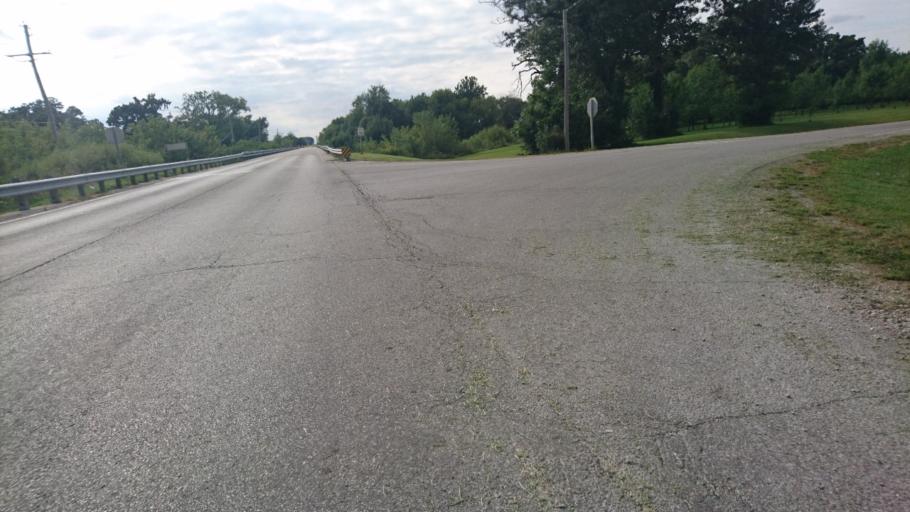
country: US
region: Illinois
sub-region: Livingston County
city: Pontiac
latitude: 40.8881
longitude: -88.6611
